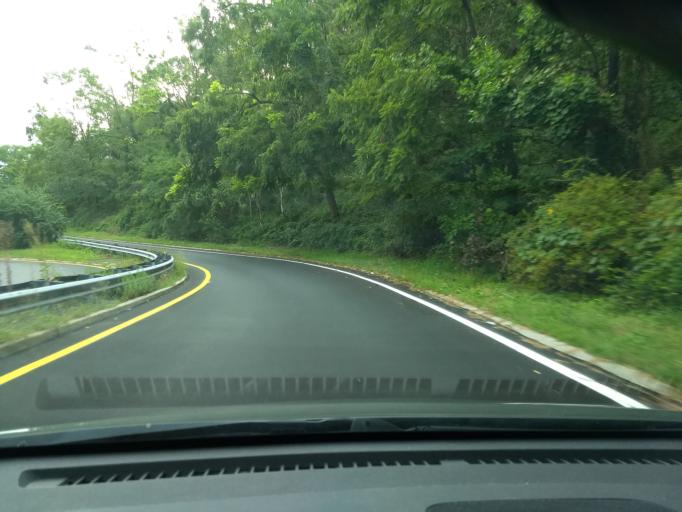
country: US
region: New York
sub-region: Nassau County
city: Lake Success
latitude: 40.7604
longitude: -73.7048
